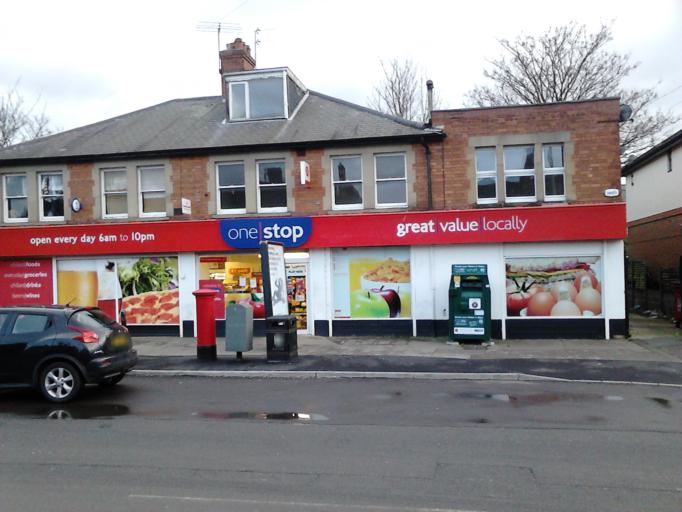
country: GB
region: England
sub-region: Nottinghamshire
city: Newark on Trent
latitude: 53.0649
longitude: -0.8044
